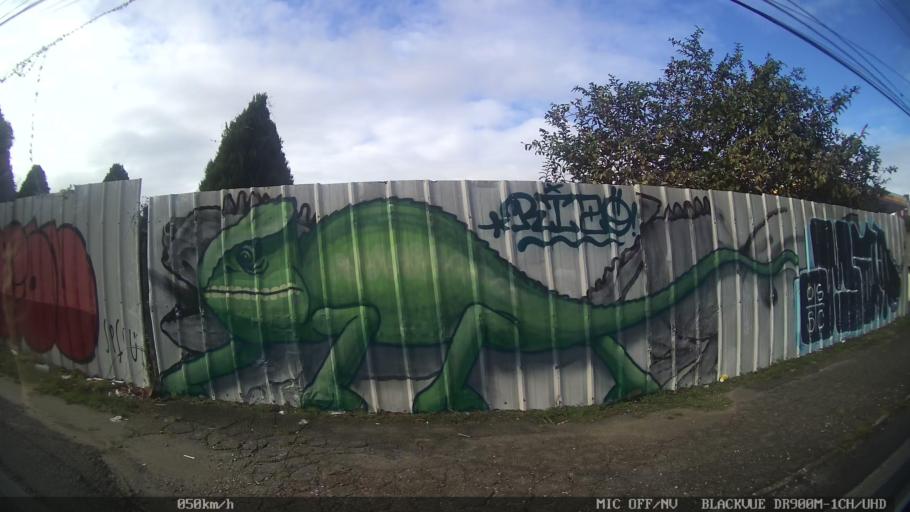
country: BR
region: Santa Catarina
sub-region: Sao Jose
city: Campinas
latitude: -27.6041
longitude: -48.6324
